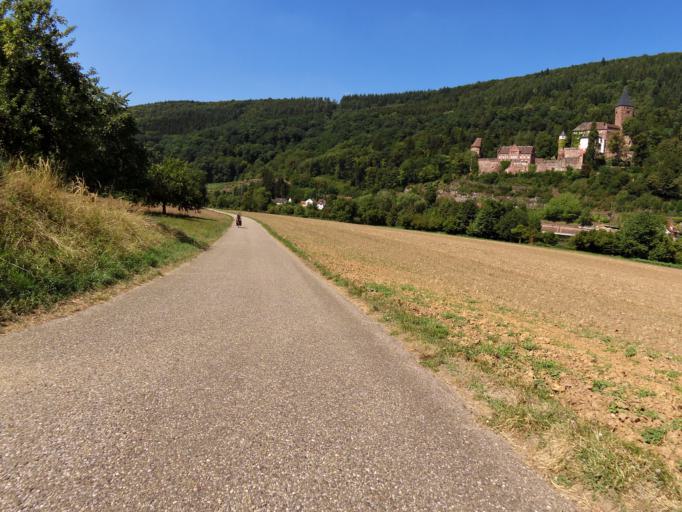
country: DE
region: Baden-Wuerttemberg
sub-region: Karlsruhe Region
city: Zwingenberg
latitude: 49.4184
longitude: 9.0361
